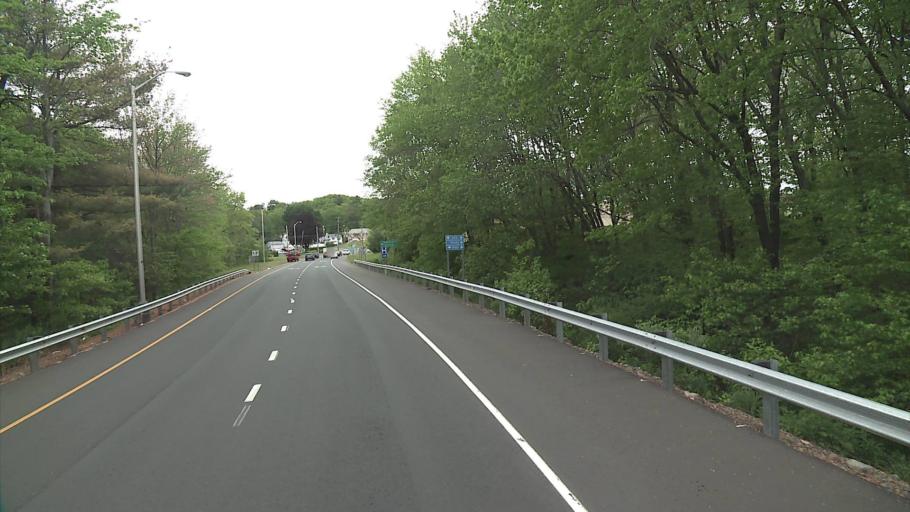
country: US
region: Connecticut
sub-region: New Haven County
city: Waterbury
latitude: 41.5506
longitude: -73.0635
